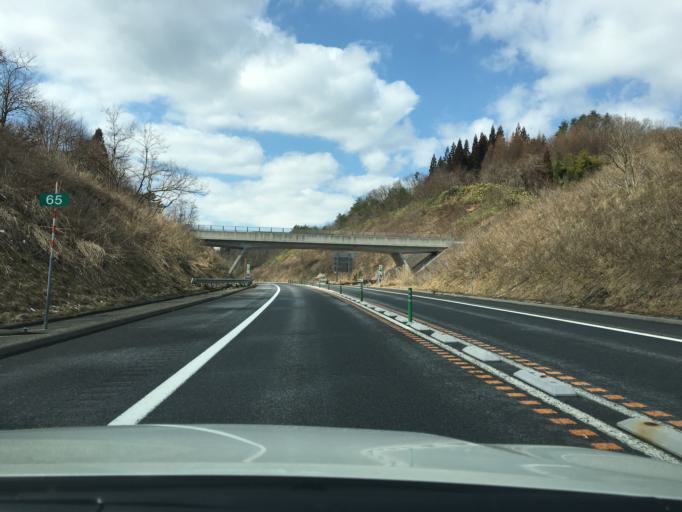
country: JP
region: Yamagata
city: Sagae
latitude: 38.4187
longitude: 140.1858
